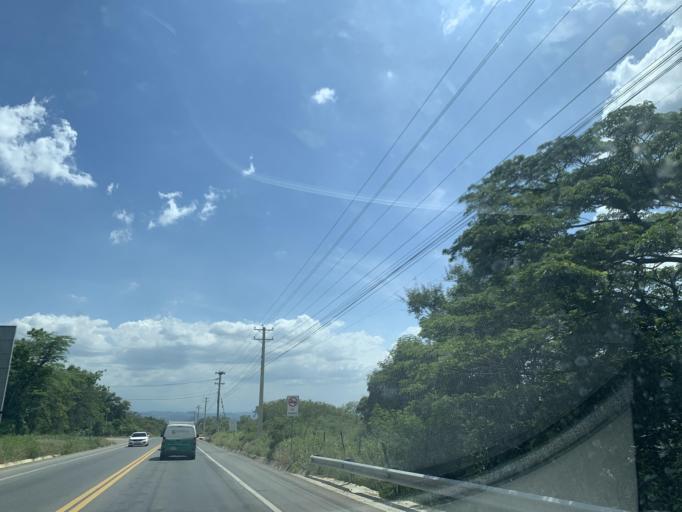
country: DO
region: Santiago
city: Villa Bisono
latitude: 19.5770
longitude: -70.8494
